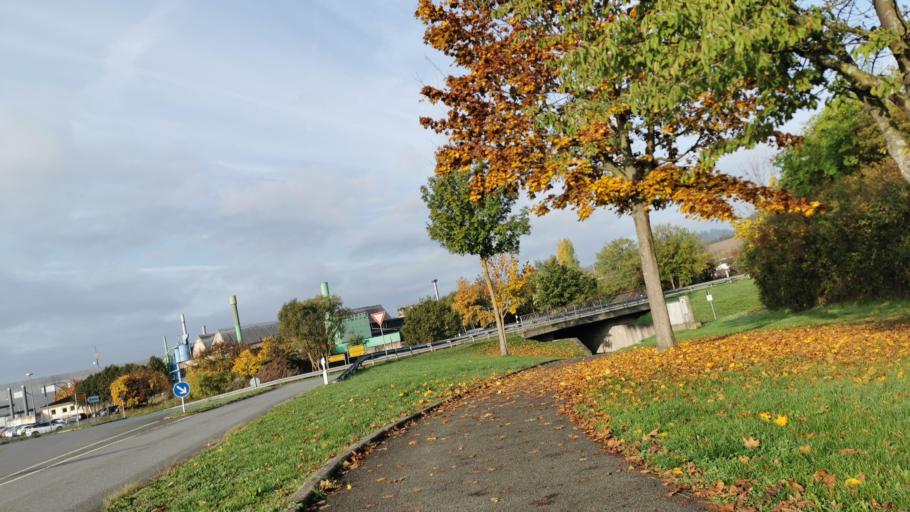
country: DE
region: Bavaria
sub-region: Upper Franconia
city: Kueps Oberfranken
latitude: 50.2098
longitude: 11.3034
